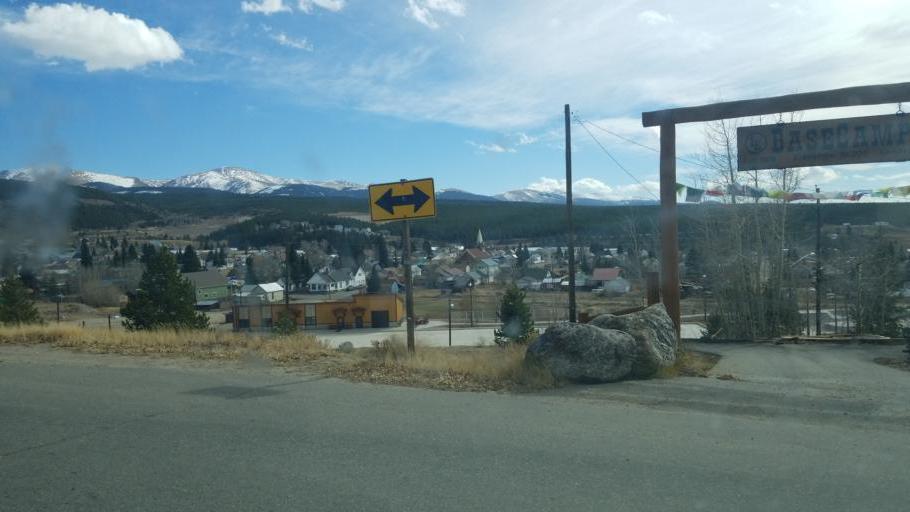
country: US
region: Colorado
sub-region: Lake County
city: Leadville
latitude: 39.2469
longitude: -106.3002
